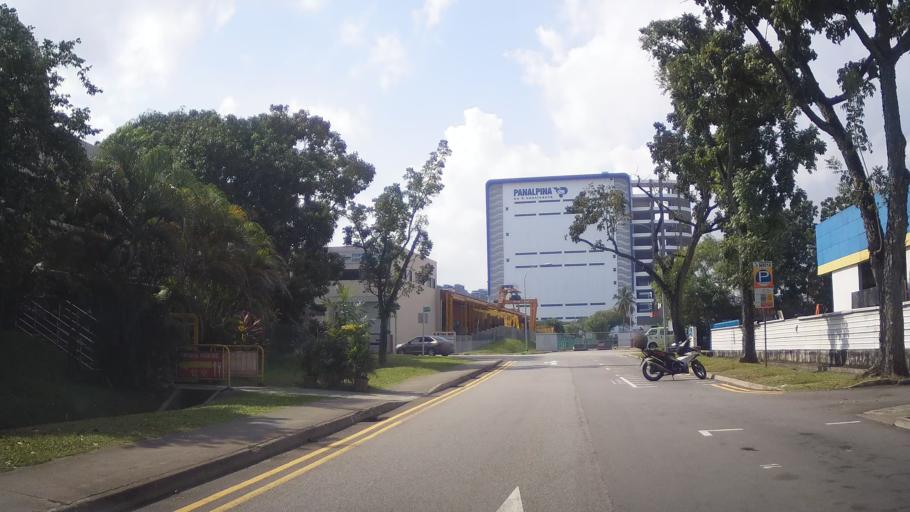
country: MY
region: Johor
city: Johor Bahru
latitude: 1.3253
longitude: 103.6993
